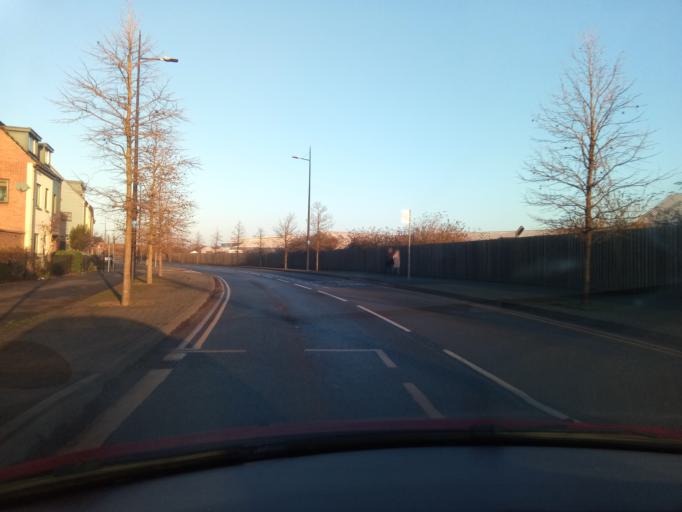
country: GB
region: England
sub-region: Leicestershire
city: Loughborough
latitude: 52.7799
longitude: -1.1982
